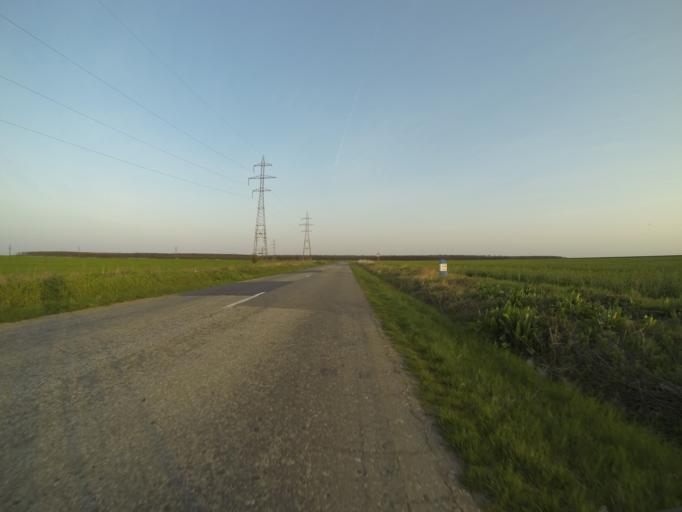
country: RO
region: Dolj
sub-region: Comuna Dranicu
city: Dranic
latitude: 44.0719
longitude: 23.7961
